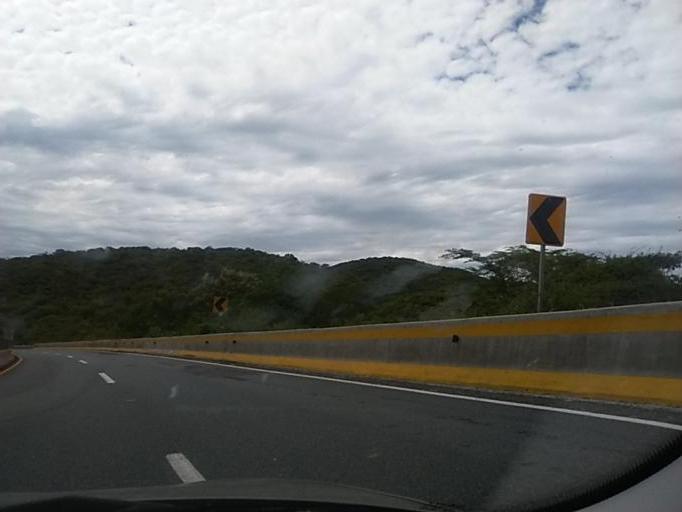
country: MX
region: Guerrero
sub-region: Huitzuco de los Figueroa
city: Ciudad de Huitzuco
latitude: 18.2563
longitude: -99.2148
